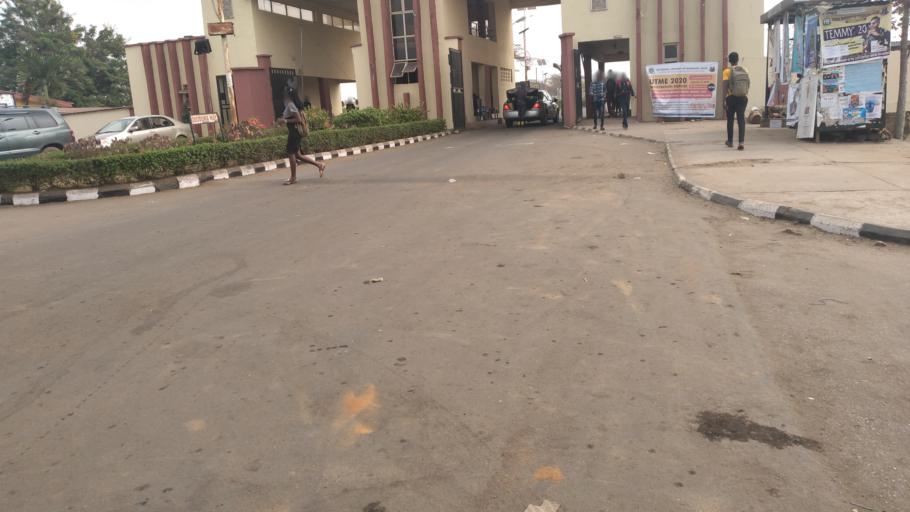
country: NG
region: Ondo
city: Ilare
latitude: 7.3069
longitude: 5.1396
